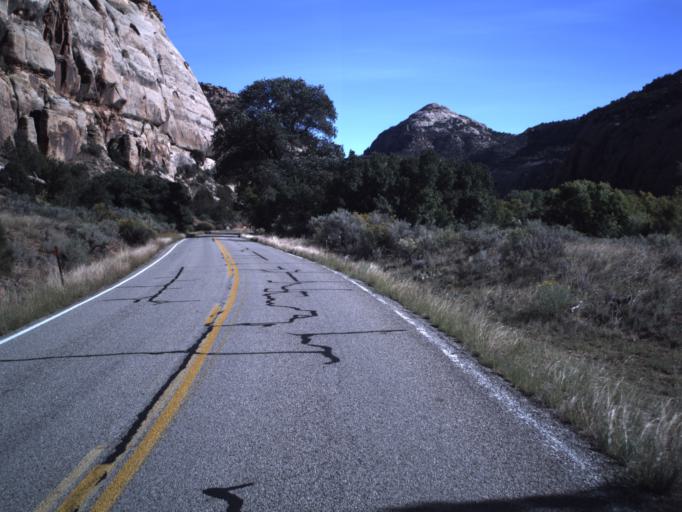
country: US
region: Utah
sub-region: San Juan County
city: Monticello
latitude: 38.0042
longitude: -109.5342
